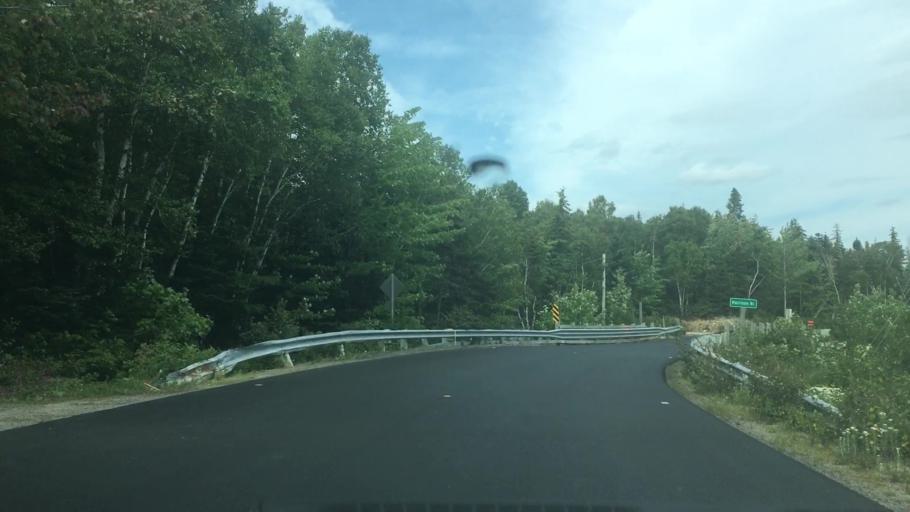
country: CA
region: Nova Scotia
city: Sydney Mines
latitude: 46.5461
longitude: -60.4154
